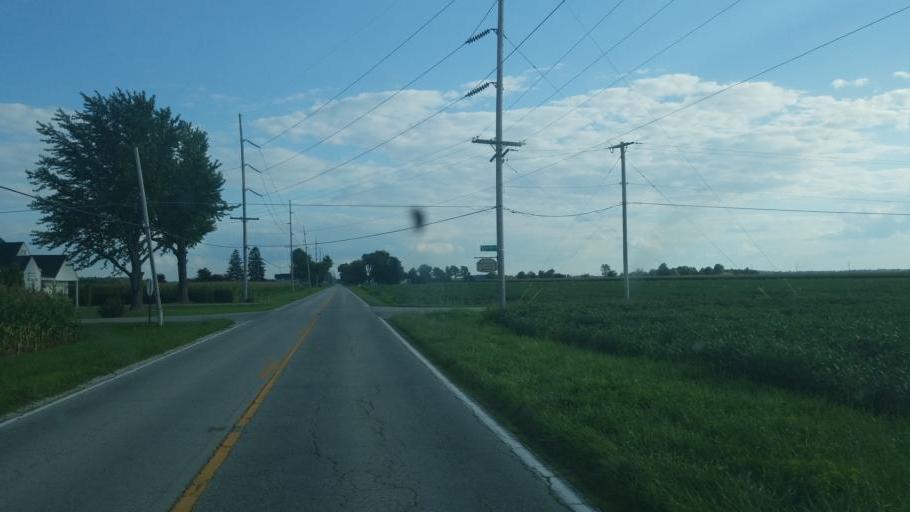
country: US
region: Ohio
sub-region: Sandusky County
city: Ballville
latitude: 41.2994
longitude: -83.1302
